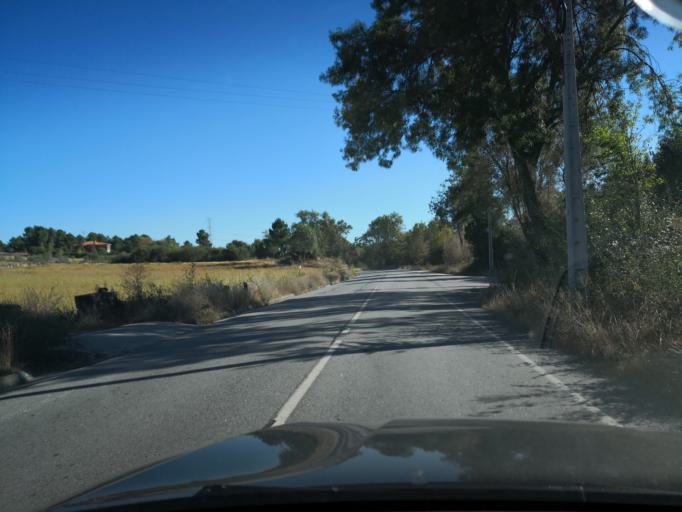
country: PT
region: Vila Real
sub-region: Valpacos
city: Valpacos
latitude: 41.6483
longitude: -7.3209
